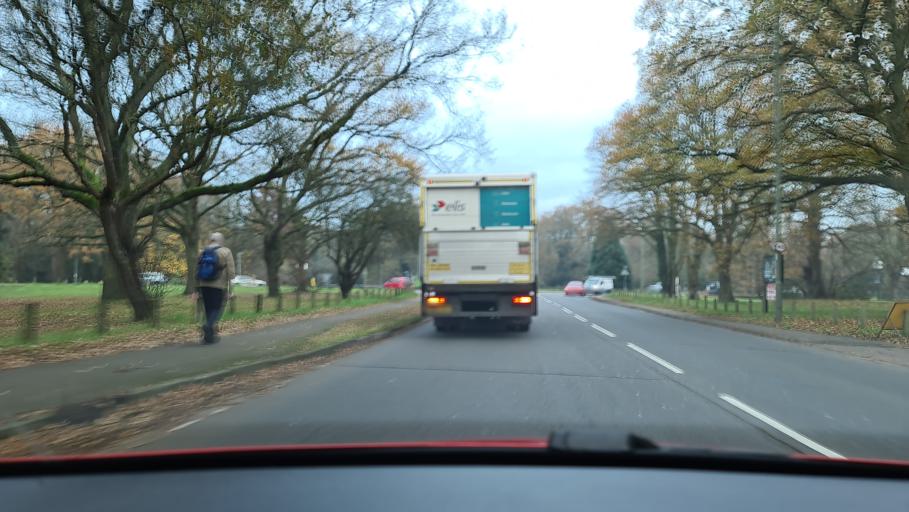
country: GB
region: England
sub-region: Surrey
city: Hinchley Wood
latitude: 51.3794
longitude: -0.3479
